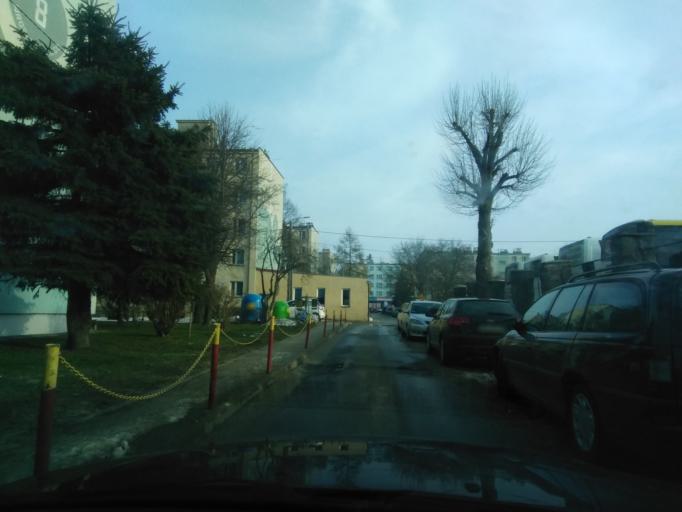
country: PL
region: Subcarpathian Voivodeship
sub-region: Krosno
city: Krosno
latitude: 49.6991
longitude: 21.7477
